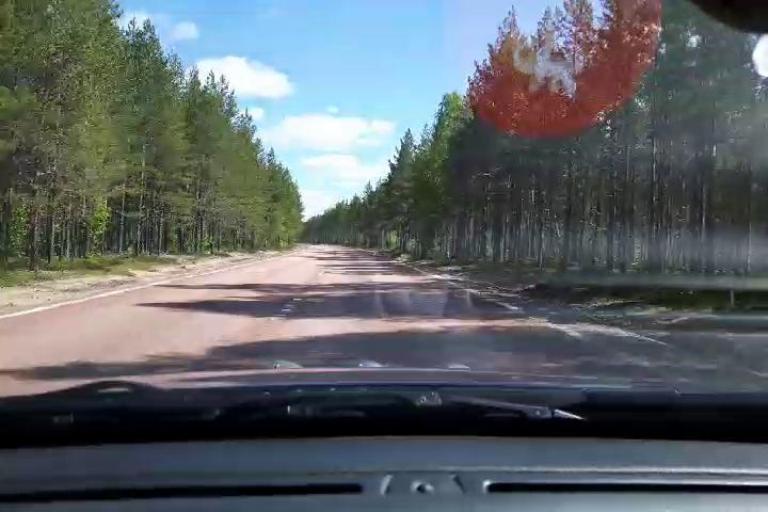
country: SE
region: Gaevleborg
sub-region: Ljusdals Kommun
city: Farila
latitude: 61.9357
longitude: 15.5159
